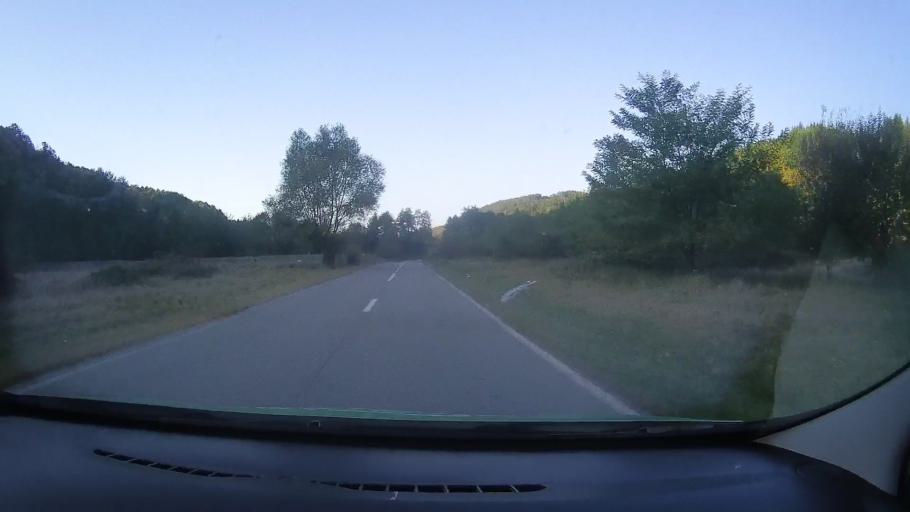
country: RO
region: Timis
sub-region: Comuna Fardea
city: Fardea
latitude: 45.7039
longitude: 22.1604
